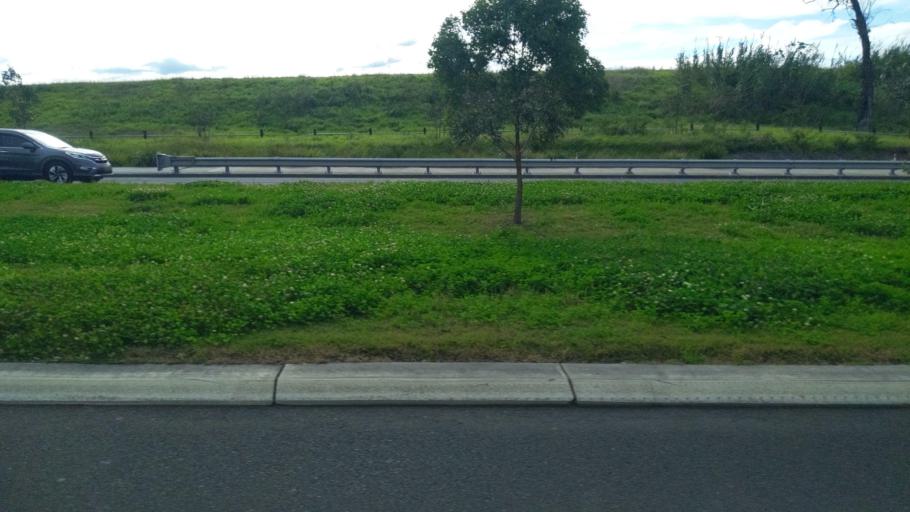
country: AU
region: New South Wales
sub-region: Blacktown
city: Riverstone
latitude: -33.7049
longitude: 150.8529
